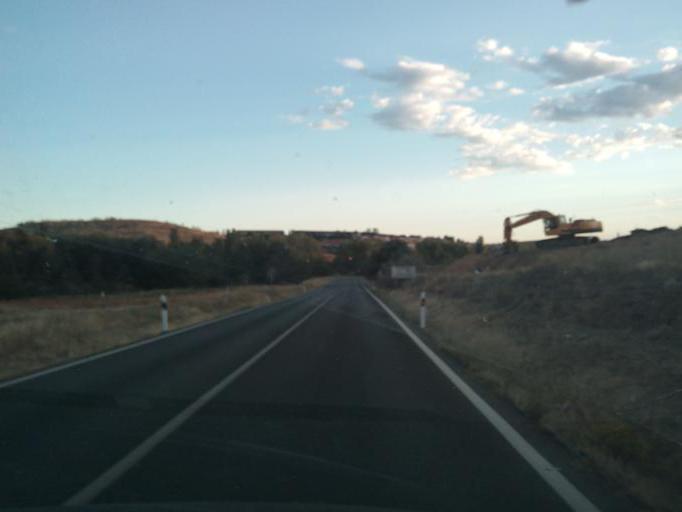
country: ES
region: Madrid
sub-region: Provincia de Madrid
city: Algete
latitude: 40.5998
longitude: -3.4907
